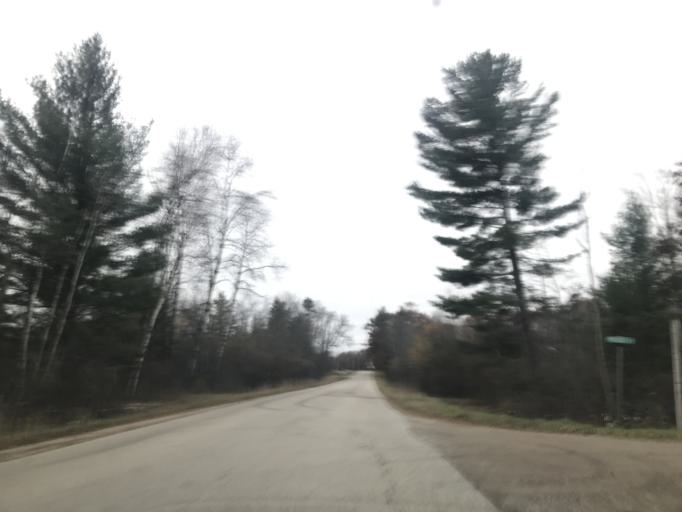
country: US
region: Wisconsin
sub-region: Marinette County
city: Peshtigo
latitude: 45.1252
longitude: -87.7499
